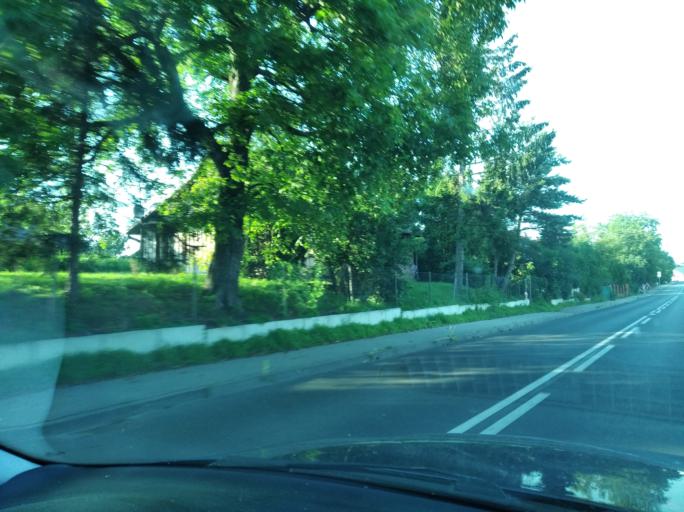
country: PL
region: Subcarpathian Voivodeship
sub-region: Powiat lezajski
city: Stare Miasto
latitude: 50.2890
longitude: 22.4297
